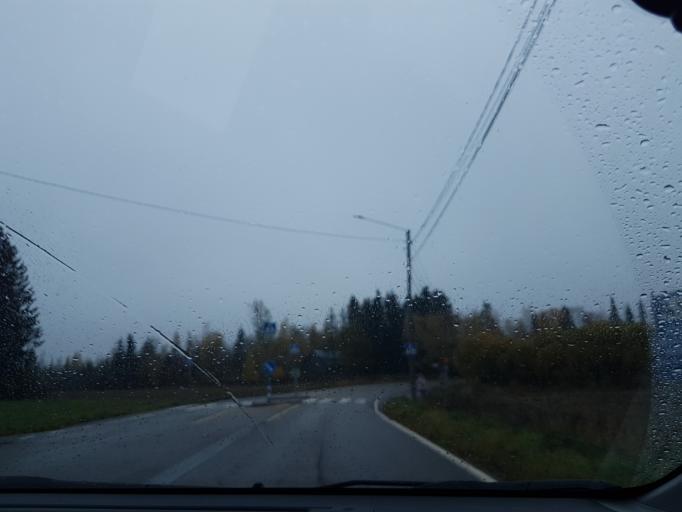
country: FI
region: Uusimaa
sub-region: Helsinki
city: Maentsaelae
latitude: 60.6171
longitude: 25.2410
